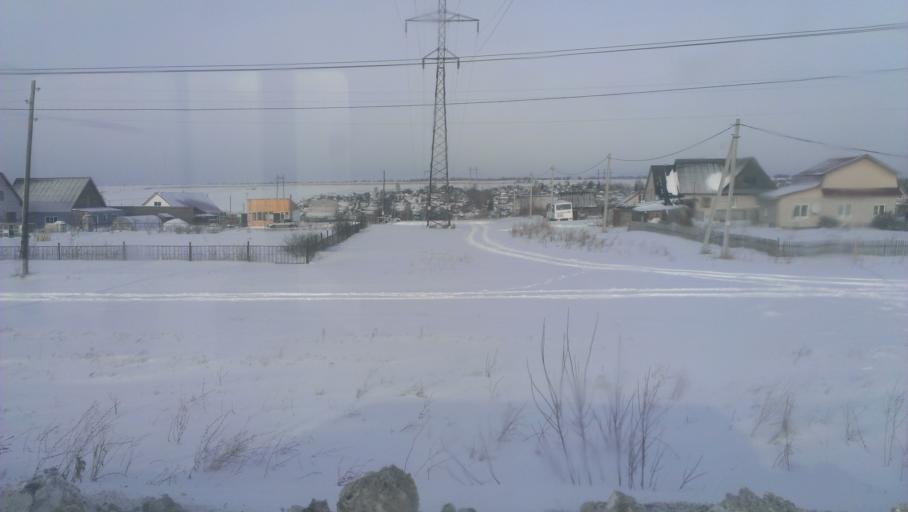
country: RU
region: Altai Krai
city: Gon'ba
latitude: 53.4124
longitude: 83.5620
